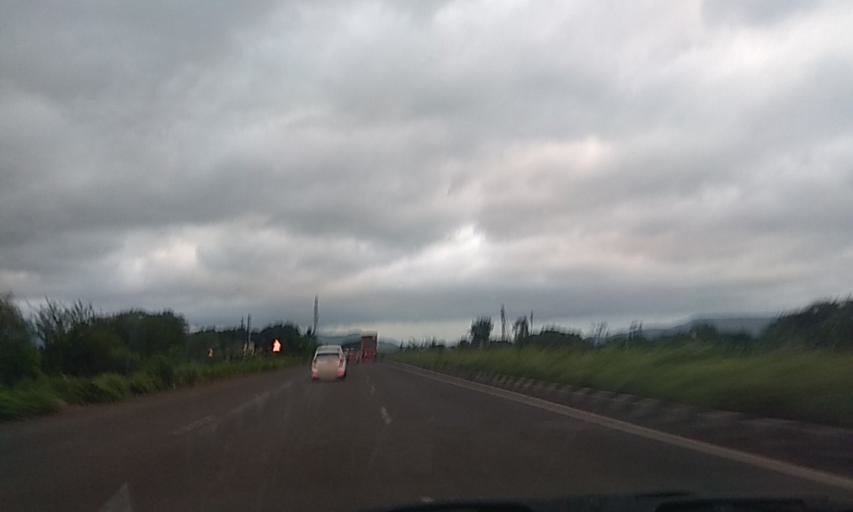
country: IN
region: Maharashtra
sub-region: Satara Division
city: Wai
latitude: 17.9412
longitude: 73.9777
